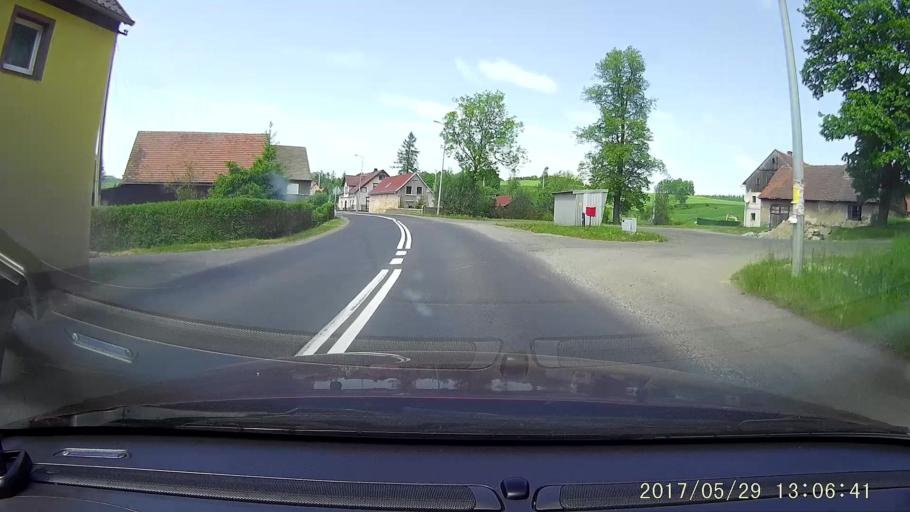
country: PL
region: Lower Silesian Voivodeship
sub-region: Powiat jeleniogorski
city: Stara Kamienica
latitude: 50.9532
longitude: 15.5799
